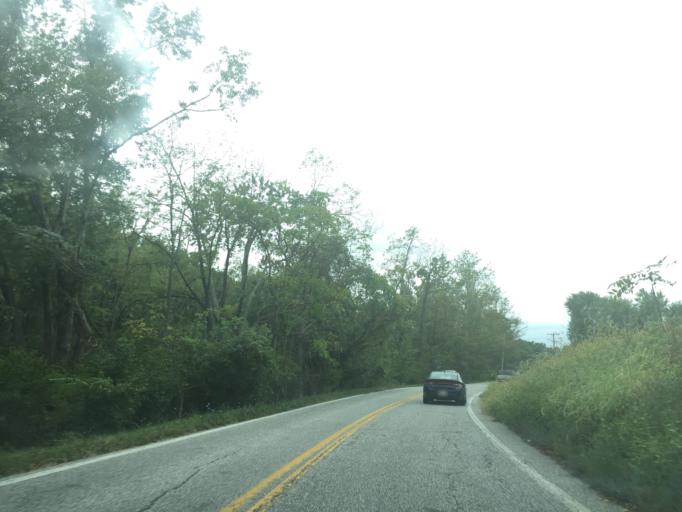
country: US
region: Maryland
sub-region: Baltimore County
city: Carney
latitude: 39.4458
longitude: -76.5075
